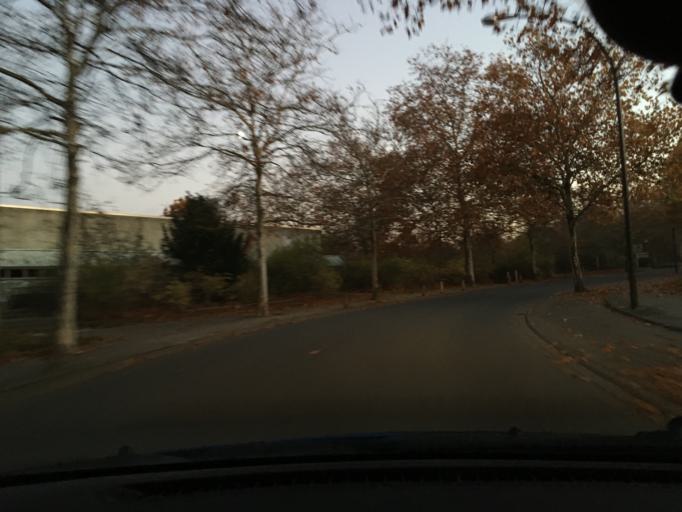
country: DE
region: Lower Saxony
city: Uelzen
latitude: 52.9555
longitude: 10.5642
